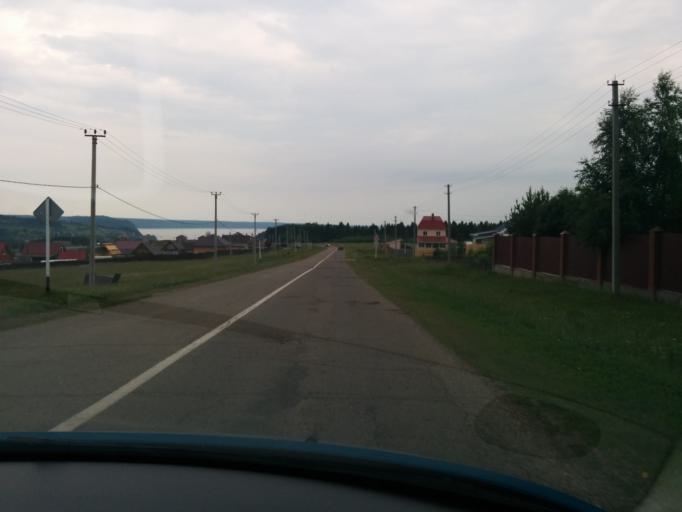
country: RU
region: Perm
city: Polazna
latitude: 58.2494
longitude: 56.2673
